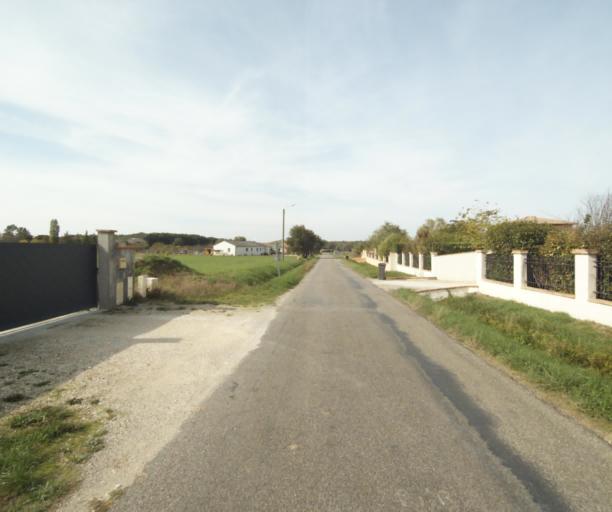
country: FR
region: Midi-Pyrenees
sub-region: Departement du Tarn-et-Garonne
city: Orgueil
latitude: 43.9018
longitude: 1.4015
